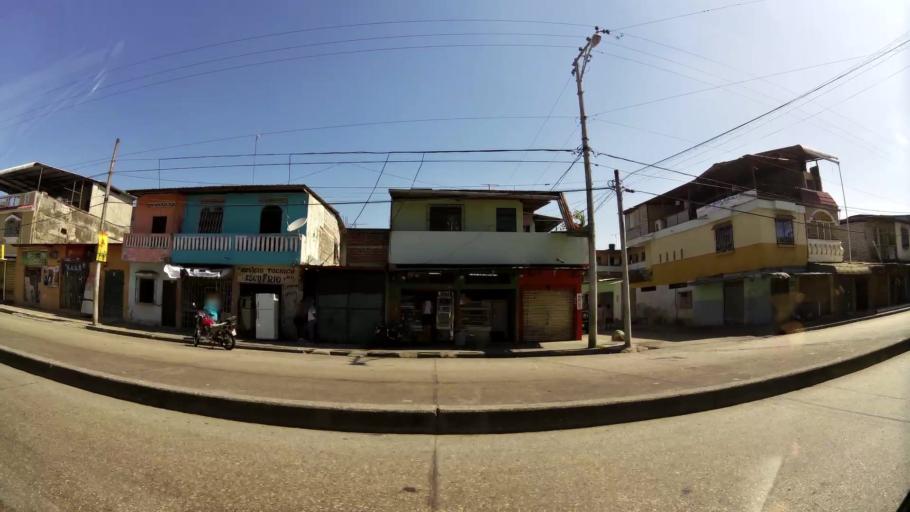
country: EC
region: Guayas
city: Guayaquil
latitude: -2.2312
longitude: -79.9398
